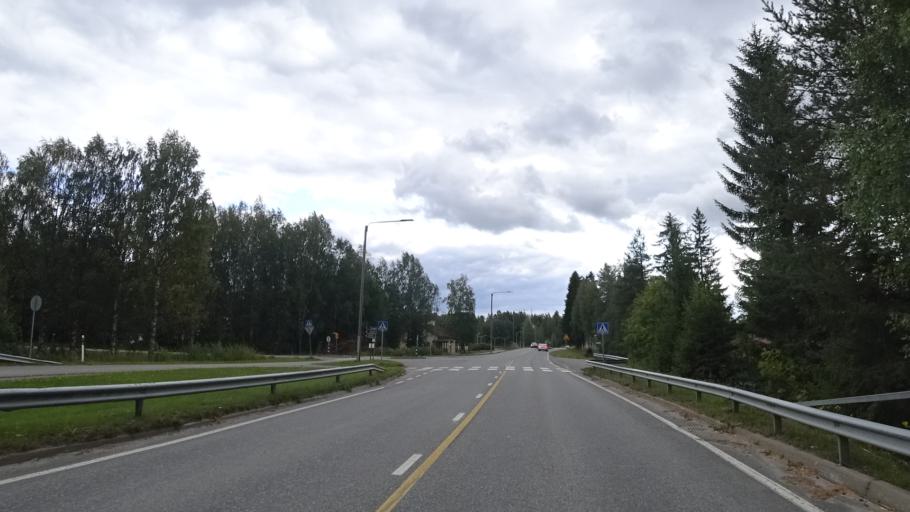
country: FI
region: North Karelia
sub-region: Joensuu
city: Ilomantsi
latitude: 62.6645
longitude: 30.9360
